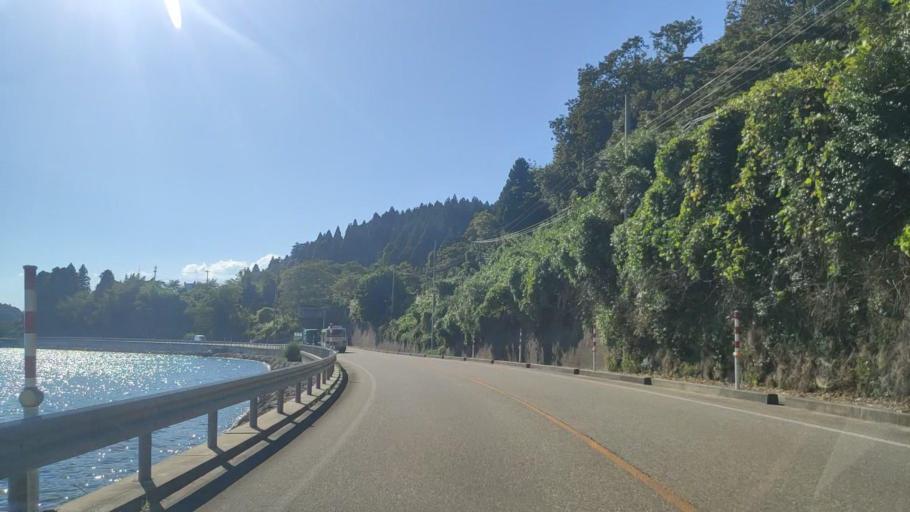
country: JP
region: Ishikawa
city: Nanao
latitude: 37.2355
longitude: 136.9557
